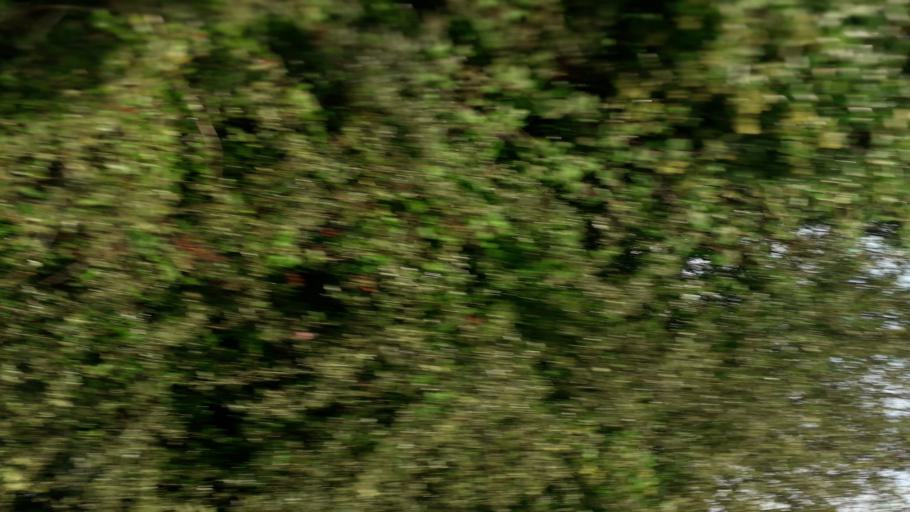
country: IE
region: Leinster
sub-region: An Longfort
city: Lanesborough
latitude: 53.7679
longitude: -8.1015
